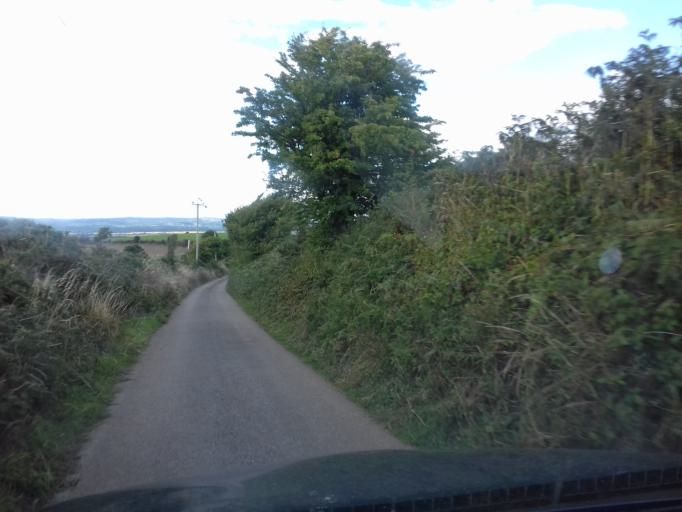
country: IE
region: Leinster
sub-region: Kilkenny
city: Graiguenamanagh
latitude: 52.5687
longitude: -7.0026
